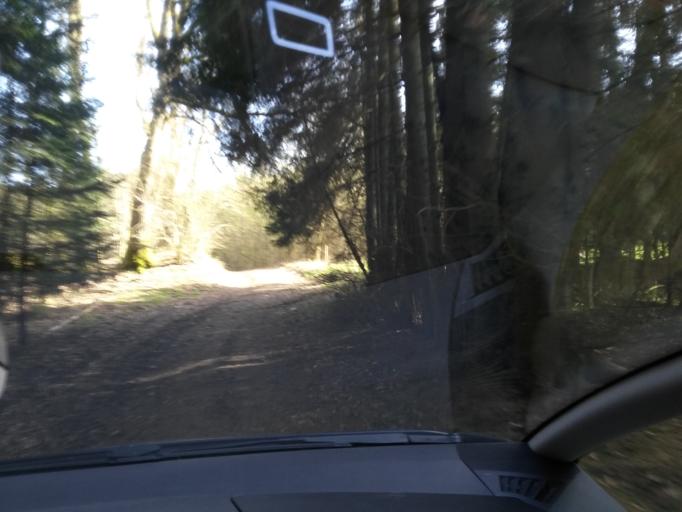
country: BE
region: Wallonia
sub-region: Province du Luxembourg
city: Daverdisse
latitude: 49.9890
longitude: 5.1593
